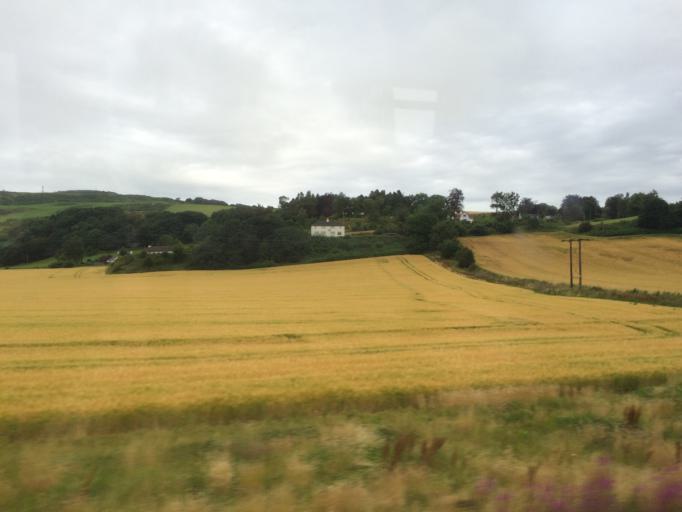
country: GB
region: Scotland
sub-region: Perth and Kinross
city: Bridge of Earn
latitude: 56.3620
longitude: -3.4368
